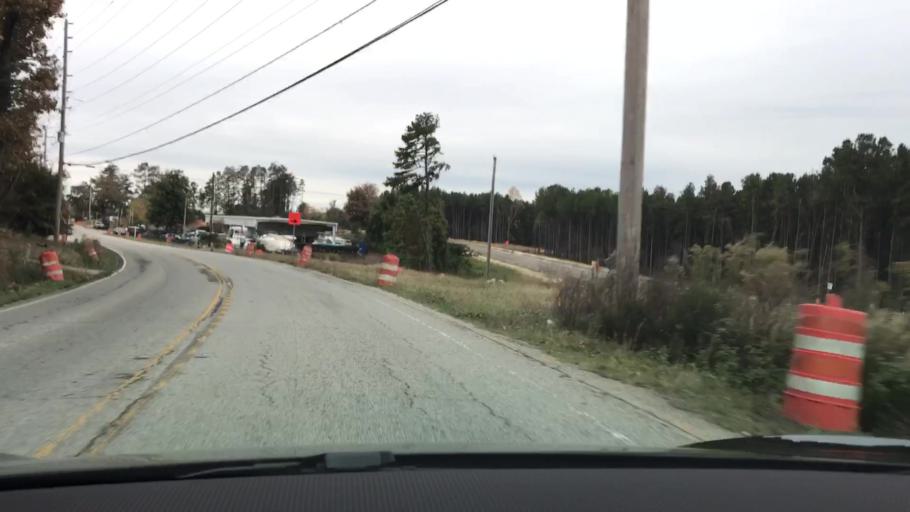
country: US
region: Georgia
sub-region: Gwinnett County
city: Buford
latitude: 34.1581
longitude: -83.9907
